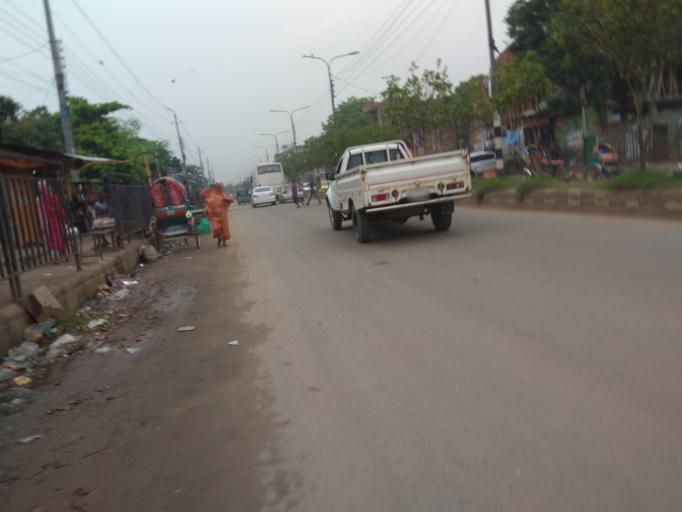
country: BD
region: Dhaka
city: Tungi
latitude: 23.8268
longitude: 90.3772
